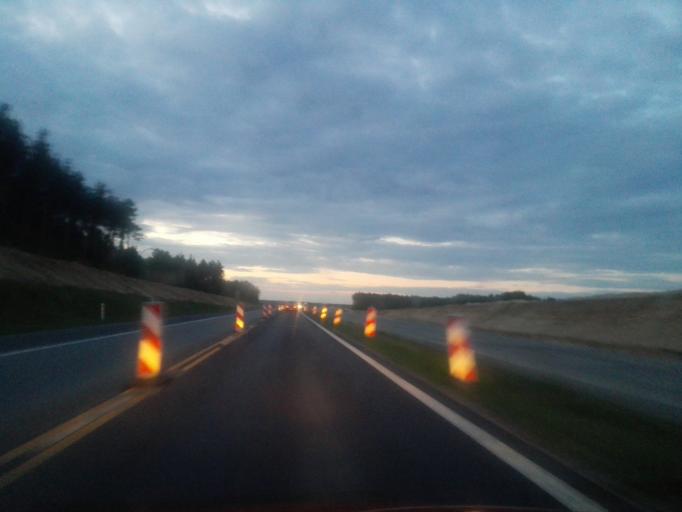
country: PL
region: Lodz Voivodeship
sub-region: Powiat piotrkowski
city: Grabica
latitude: 51.5357
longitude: 19.6006
